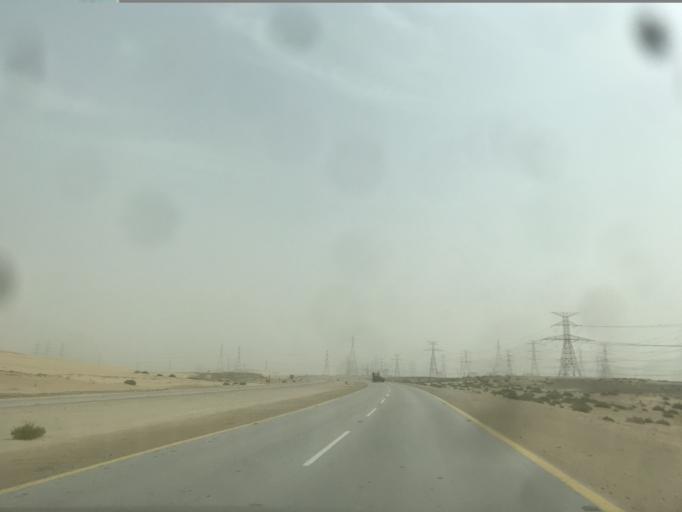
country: SA
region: Eastern Province
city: Abqaiq
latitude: 25.9077
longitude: 49.8895
